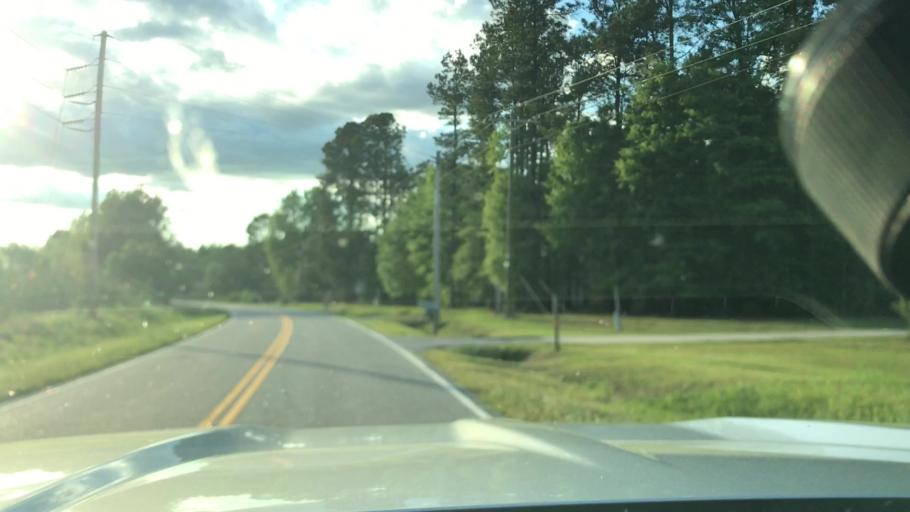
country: US
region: South Carolina
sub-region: Barnwell County
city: Blackville
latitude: 33.4736
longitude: -81.1740
